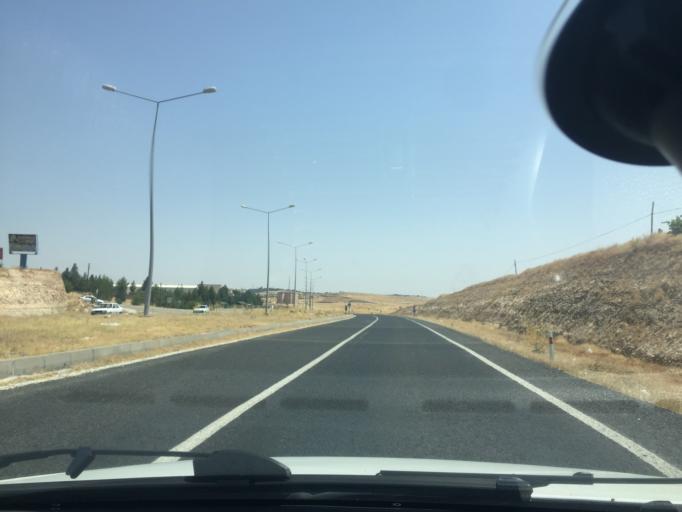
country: TR
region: Mardin
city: Acirli
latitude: 37.4395
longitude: 41.2948
